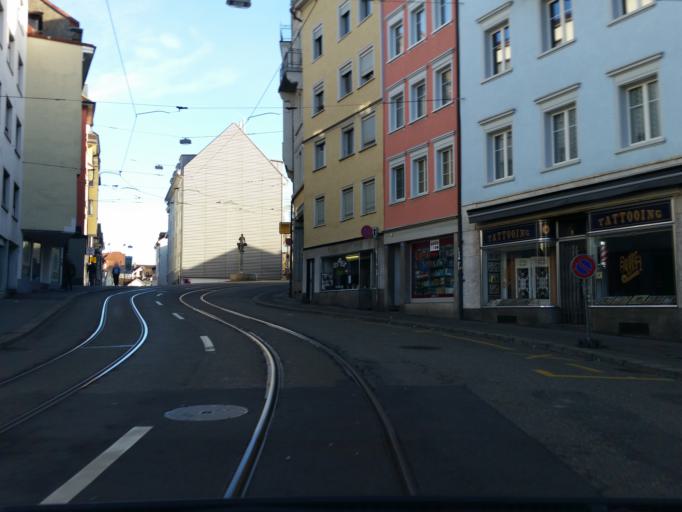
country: CH
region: Saint Gallen
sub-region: Wahlkreis St. Gallen
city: Sankt Gallen
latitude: 47.4244
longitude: 9.3814
